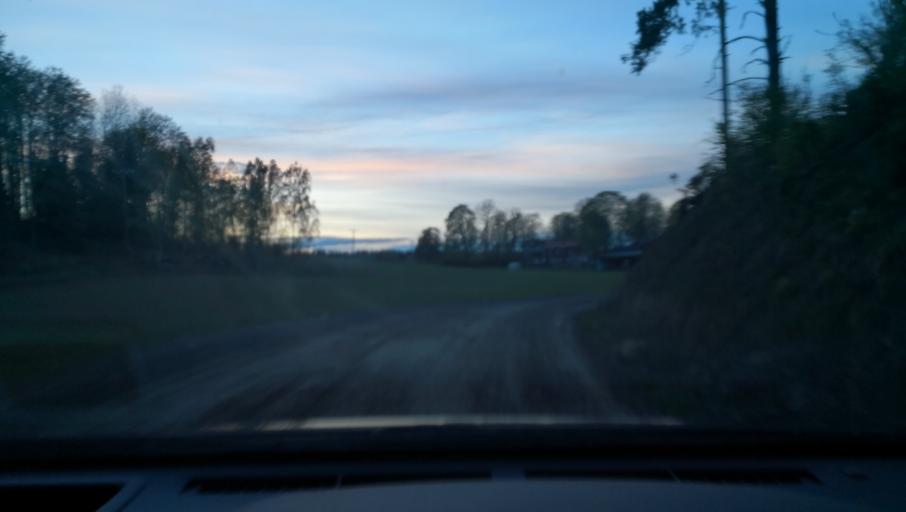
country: SE
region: OErebro
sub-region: Askersunds Kommun
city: Askersund
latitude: 58.9934
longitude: 14.9034
